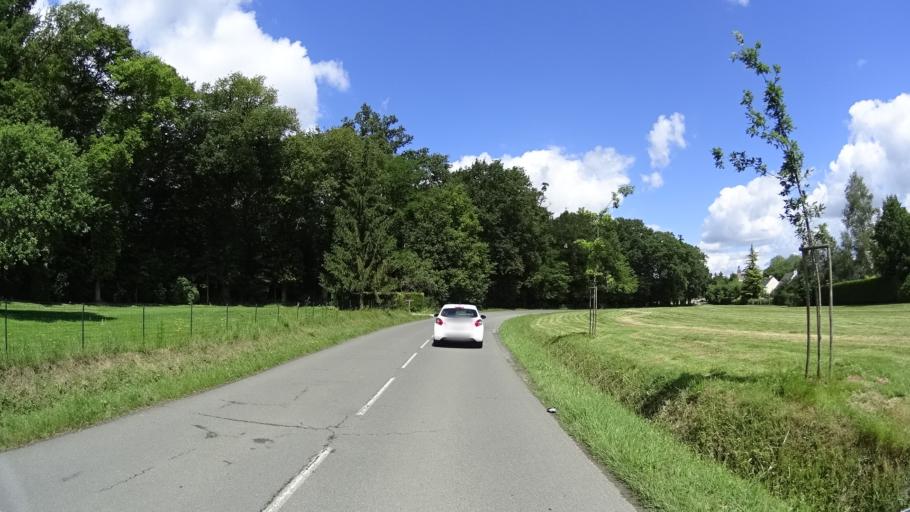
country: FR
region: Brittany
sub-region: Departement d'Ille-et-Vilaine
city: Saint-Gilles
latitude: 48.1486
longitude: -1.8303
